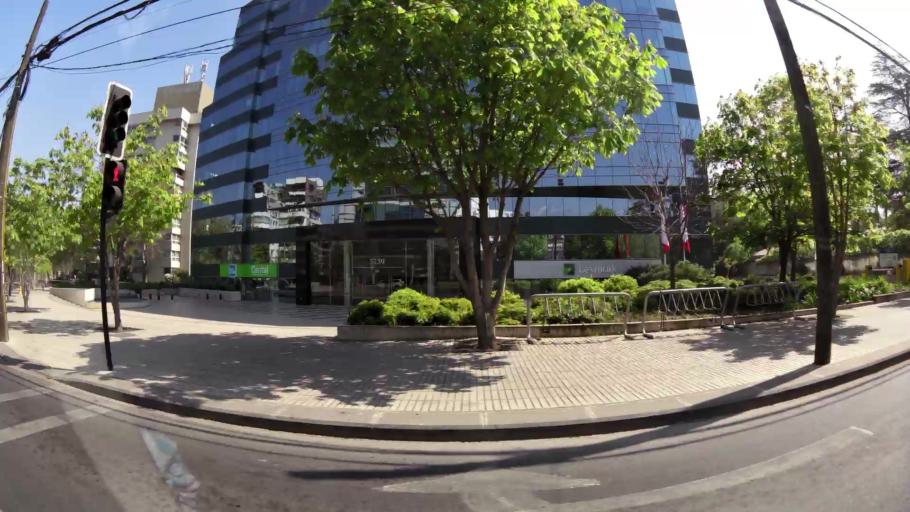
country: CL
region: Santiago Metropolitan
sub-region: Provincia de Santiago
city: Villa Presidente Frei, Nunoa, Santiago, Chile
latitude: -33.3971
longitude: -70.5836
